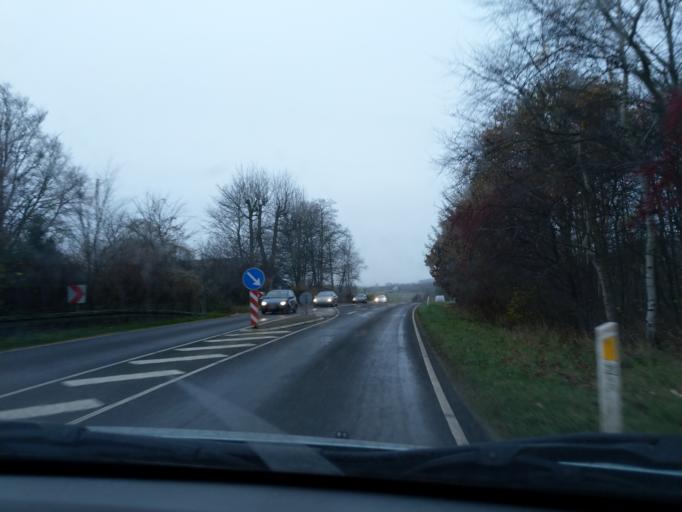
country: DK
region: Zealand
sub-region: Vordingborg Kommune
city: Praesto
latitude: 55.1169
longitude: 11.9962
